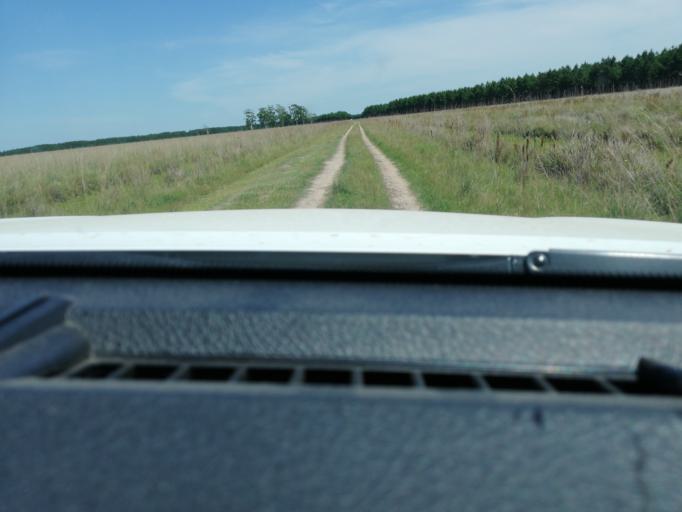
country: AR
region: Corrientes
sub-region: Departamento de San Miguel
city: San Miguel
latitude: -28.0404
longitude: -57.4609
